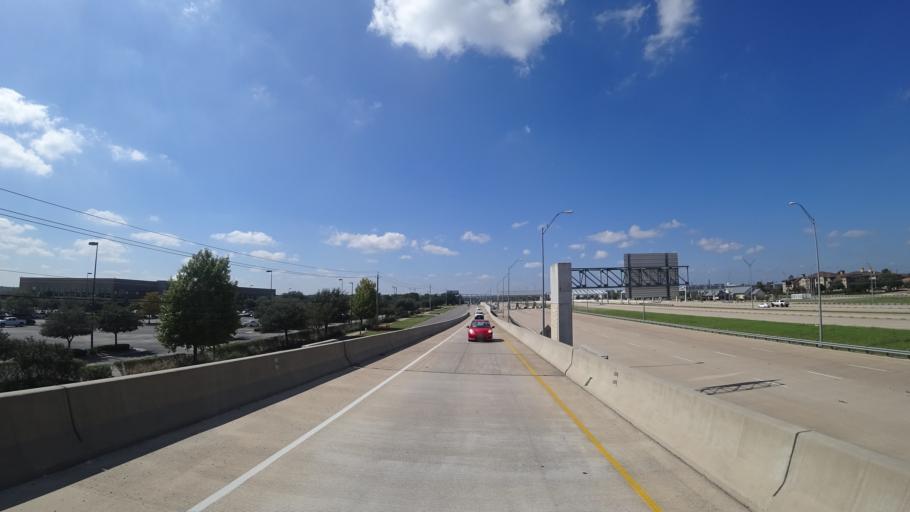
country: US
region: Texas
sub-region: Williamson County
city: Jollyville
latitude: 30.4739
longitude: -97.7730
